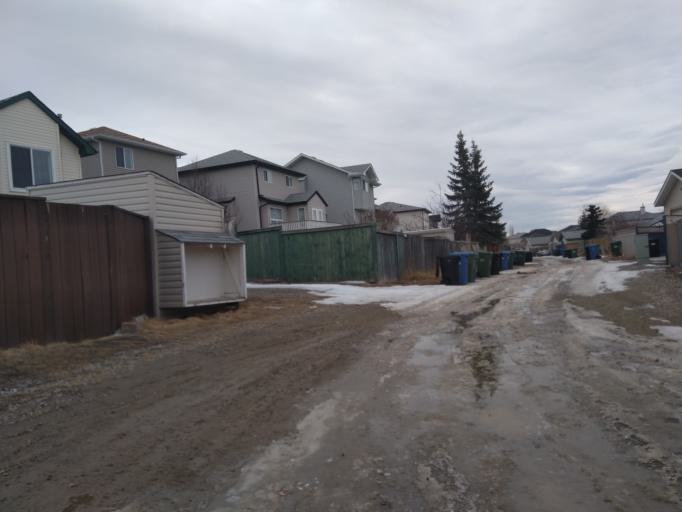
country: CA
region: Alberta
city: Calgary
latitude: 51.1682
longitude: -114.0440
